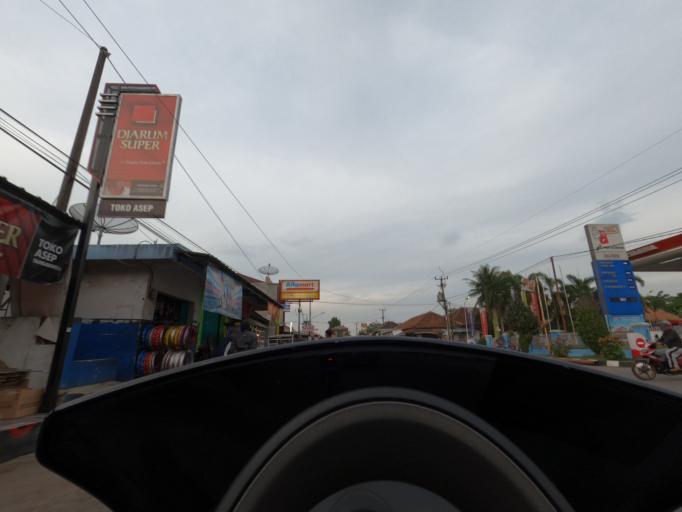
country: ID
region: West Java
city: Lembang
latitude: -6.6559
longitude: 107.7155
